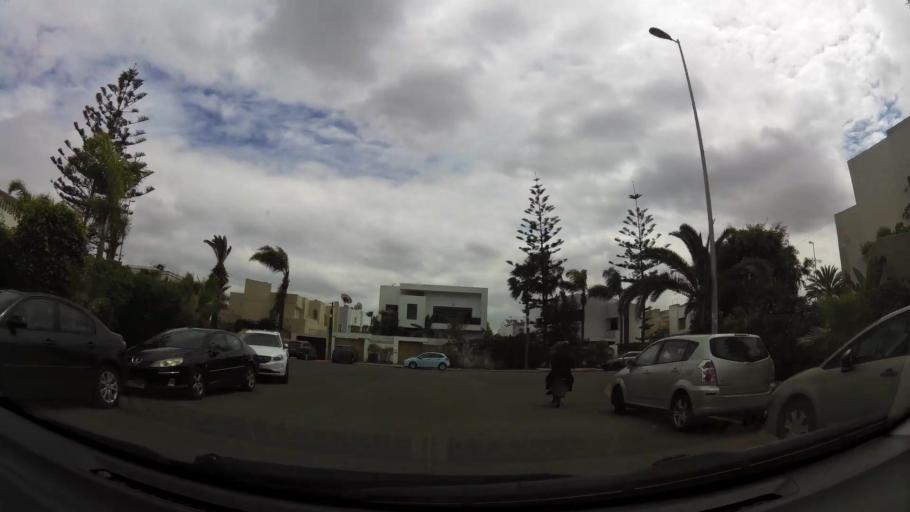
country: MA
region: Grand Casablanca
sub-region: Casablanca
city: Casablanca
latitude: 33.5727
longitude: -7.6639
